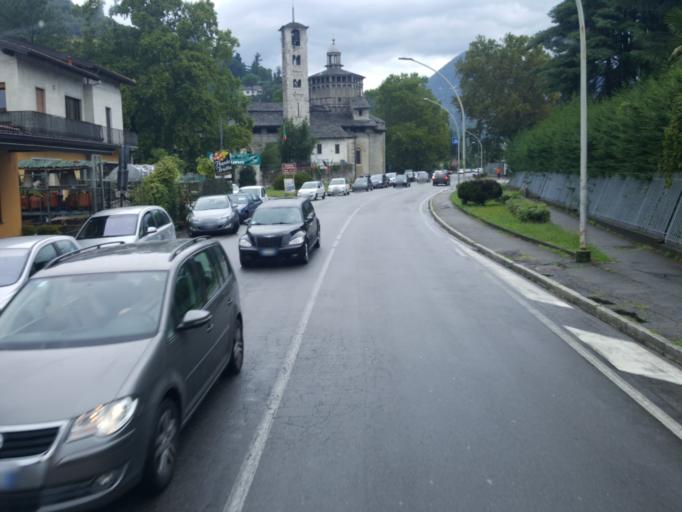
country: IT
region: Piedmont
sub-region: Provincia Verbano-Cusio-Ossola
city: Verbania
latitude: 45.9315
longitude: 8.5533
